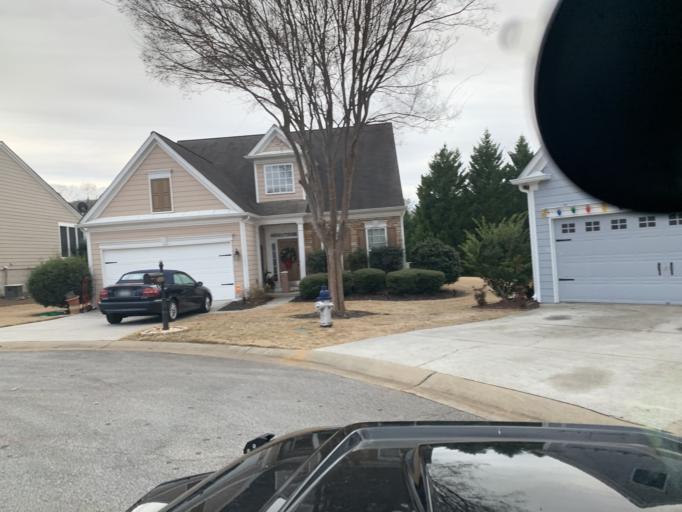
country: US
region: Georgia
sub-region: Cherokee County
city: Woodstock
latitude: 34.0884
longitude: -84.4562
